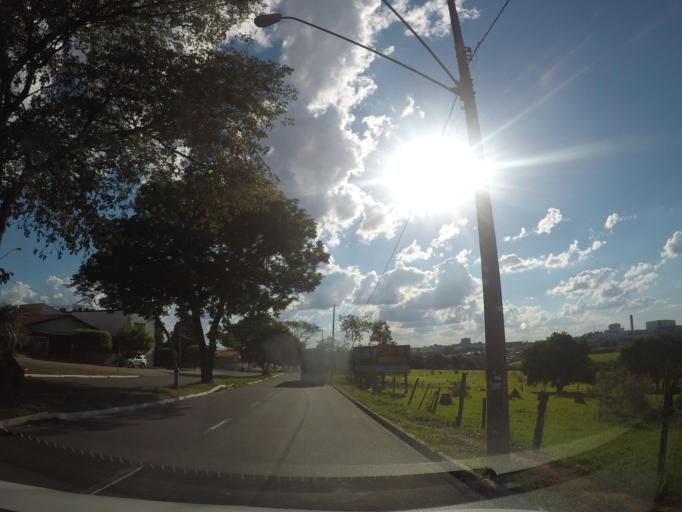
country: BR
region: Sao Paulo
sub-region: Sumare
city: Sumare
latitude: -22.8063
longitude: -47.2250
